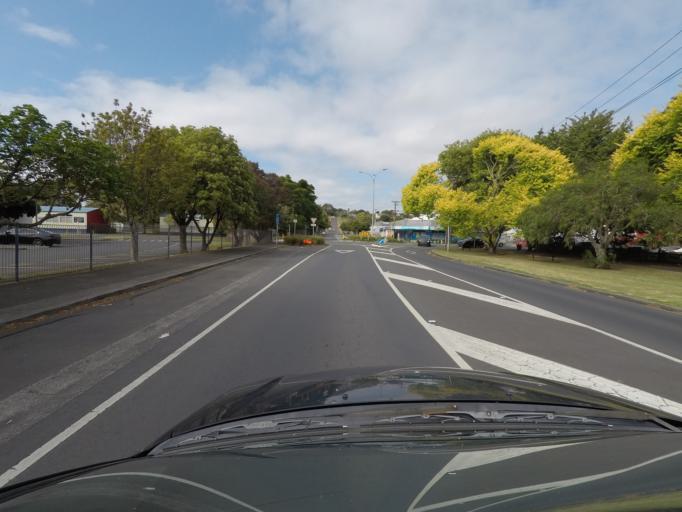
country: NZ
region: Auckland
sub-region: Auckland
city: Auckland
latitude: -36.9122
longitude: 174.7481
